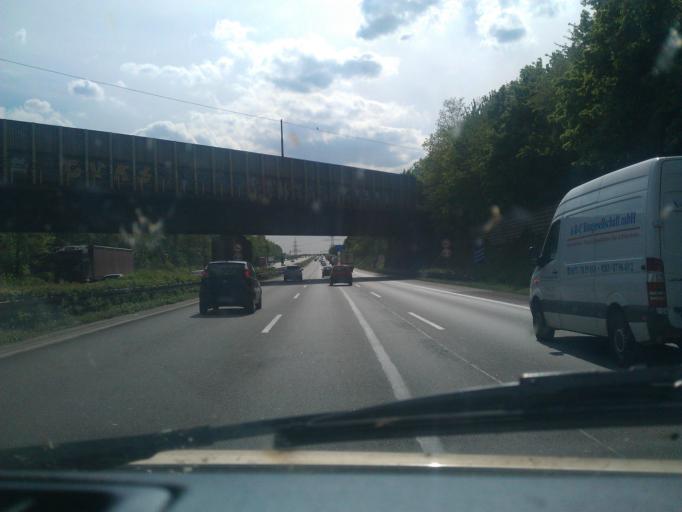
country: DE
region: North Rhine-Westphalia
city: Meiderich
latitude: 51.4853
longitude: 6.7421
